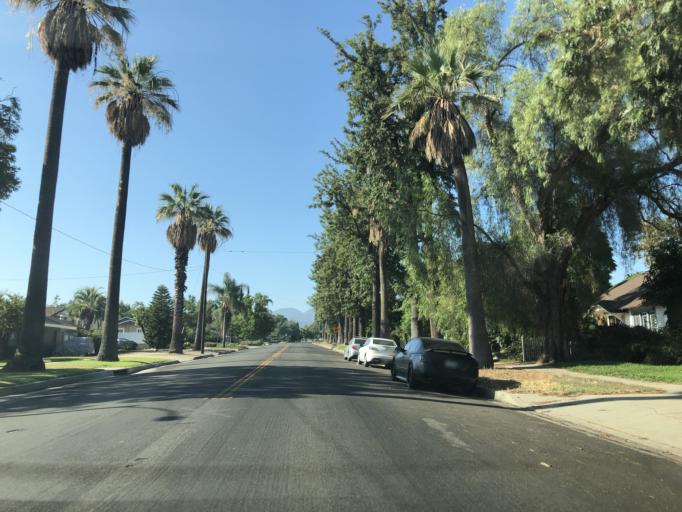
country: US
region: California
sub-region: Riverside County
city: Corona
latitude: 33.8689
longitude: -117.5618
